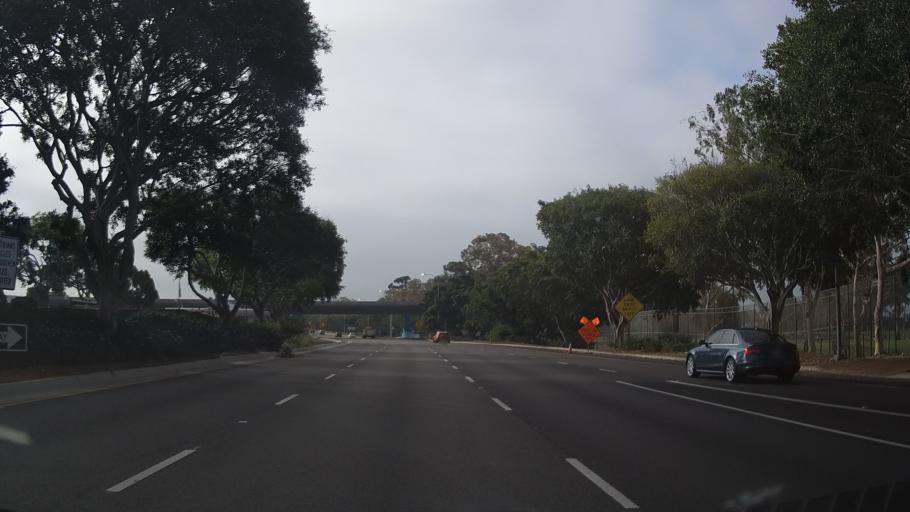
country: US
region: California
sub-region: San Diego County
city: Coronado
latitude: 32.6915
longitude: -117.1684
